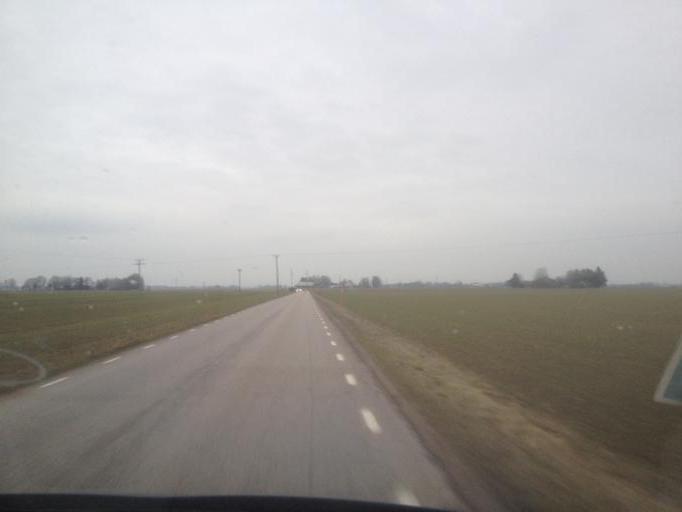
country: SE
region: OEstergoetland
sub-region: Linkopings Kommun
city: Vikingstad
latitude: 58.4218
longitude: 15.4200
